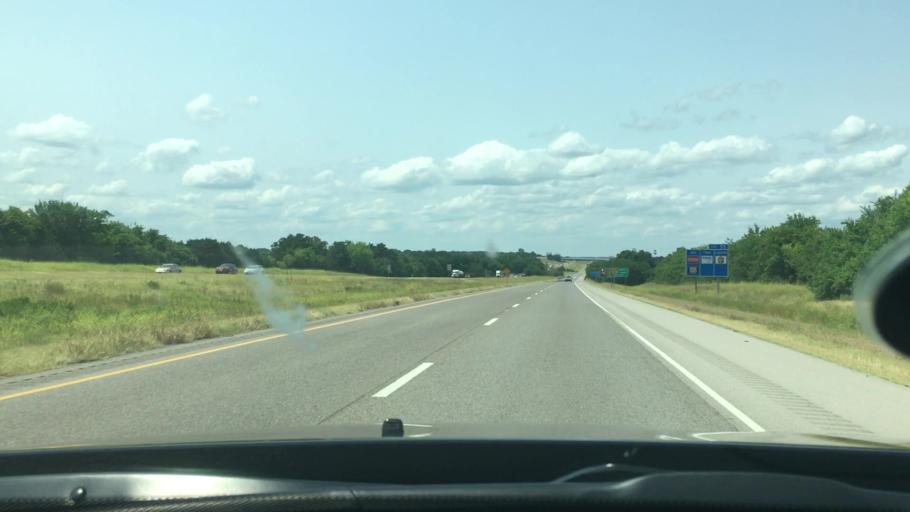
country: US
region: Oklahoma
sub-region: Murray County
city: Davis
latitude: 34.4938
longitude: -97.1652
